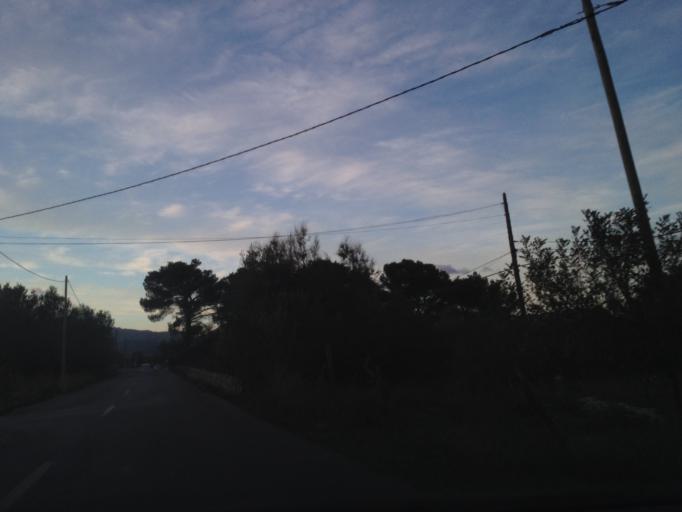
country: ES
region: Balearic Islands
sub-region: Illes Balears
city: Pollenca
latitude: 39.8554
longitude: 3.0569
